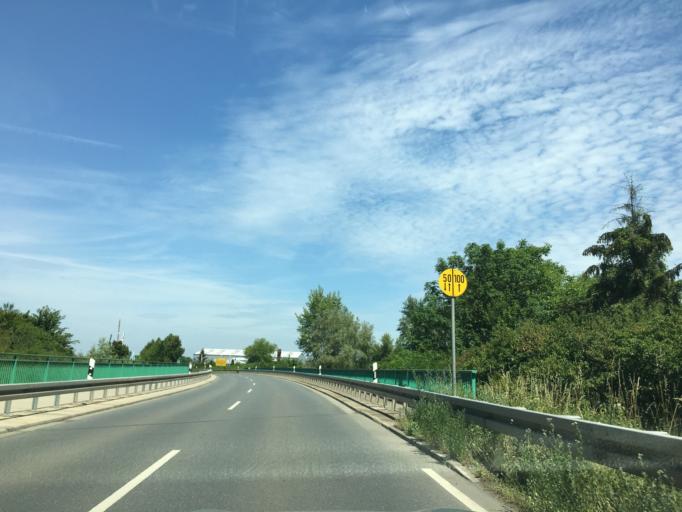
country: DE
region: Hesse
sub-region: Regierungsbezirk Darmstadt
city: Stockstadt am Rhein
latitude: 49.8208
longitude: 8.4801
